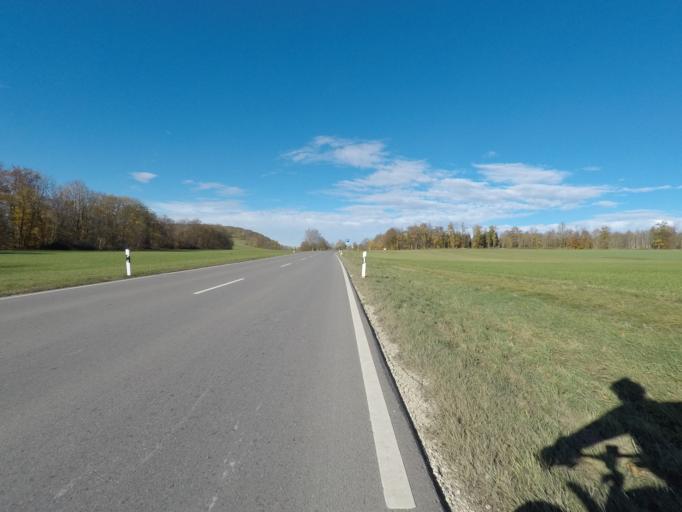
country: DE
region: Baden-Wuerttemberg
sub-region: Tuebingen Region
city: Pfullingen
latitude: 48.4207
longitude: 9.2097
